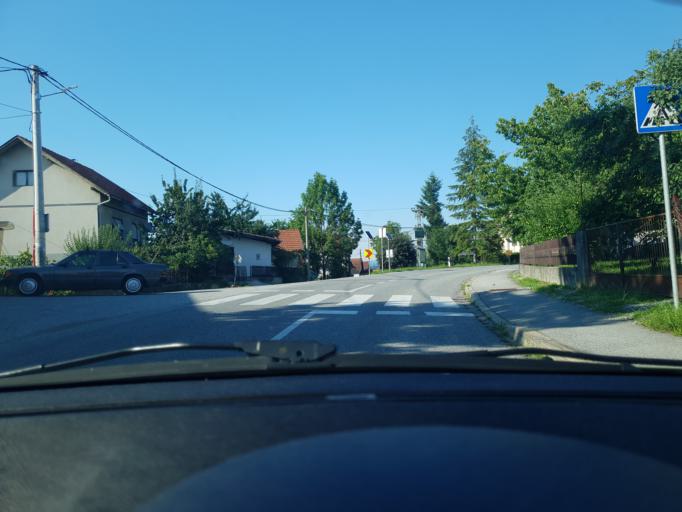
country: HR
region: Krapinsko-Zagorska
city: Oroslavje
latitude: 45.9796
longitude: 15.8953
